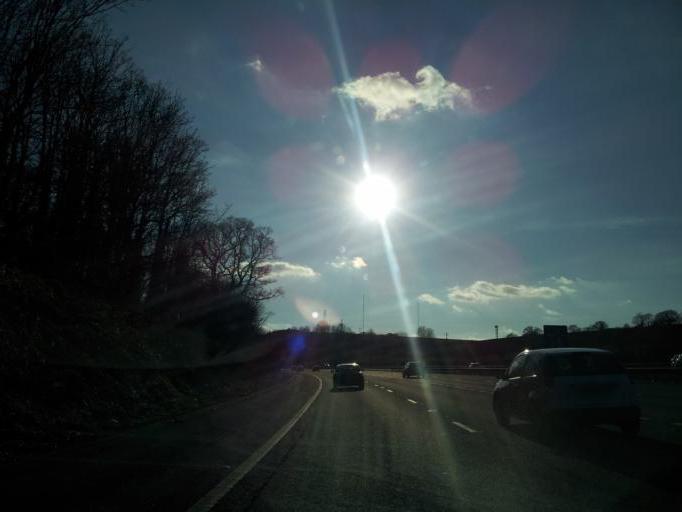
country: GB
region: England
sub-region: Devon
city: Exminster
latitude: 50.6850
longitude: -3.5066
